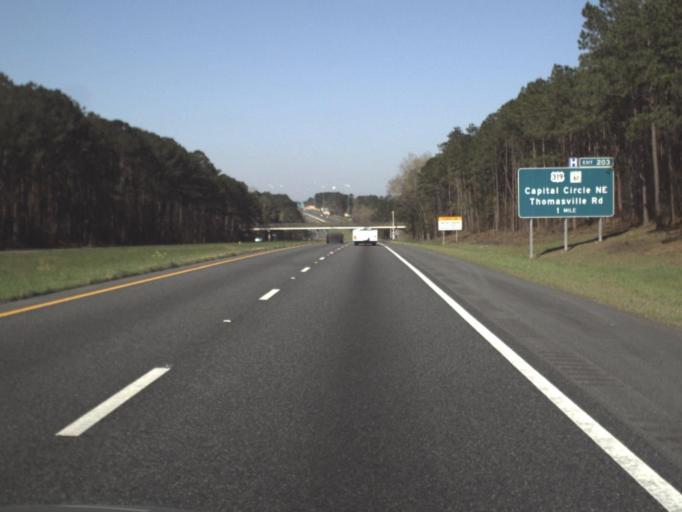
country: US
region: Florida
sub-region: Leon County
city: Tallahassee
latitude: 30.5007
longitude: -84.2254
